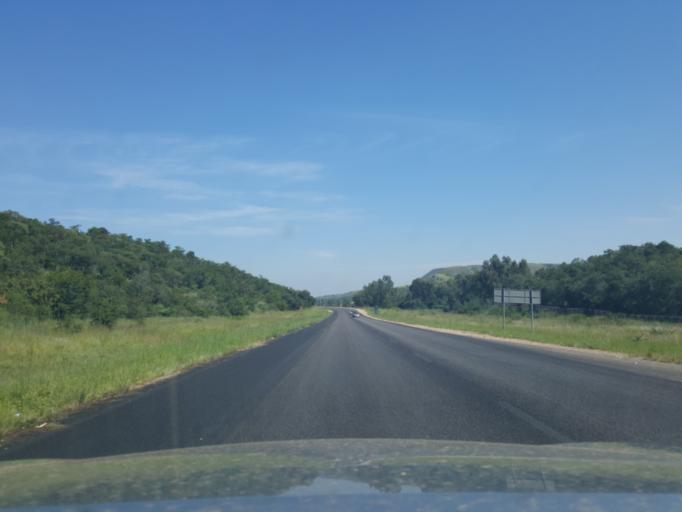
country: ZA
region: Gauteng
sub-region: City of Tshwane Metropolitan Municipality
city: Cullinan
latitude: -25.6814
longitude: 28.5096
